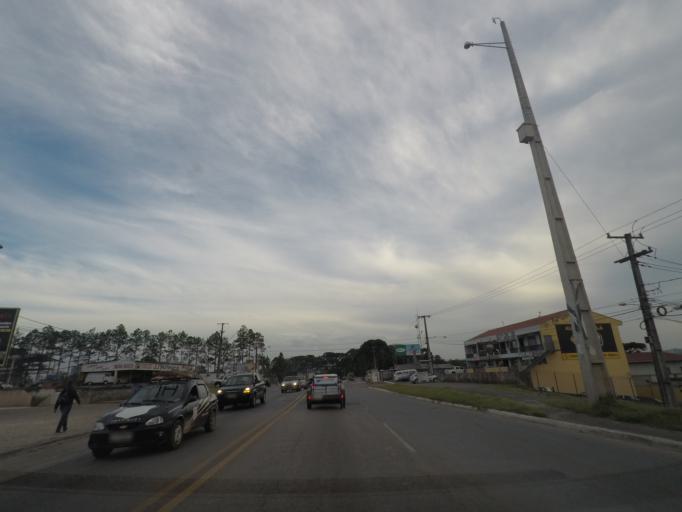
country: BR
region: Parana
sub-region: Colombo
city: Colombo
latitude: -25.3462
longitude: -49.2200
